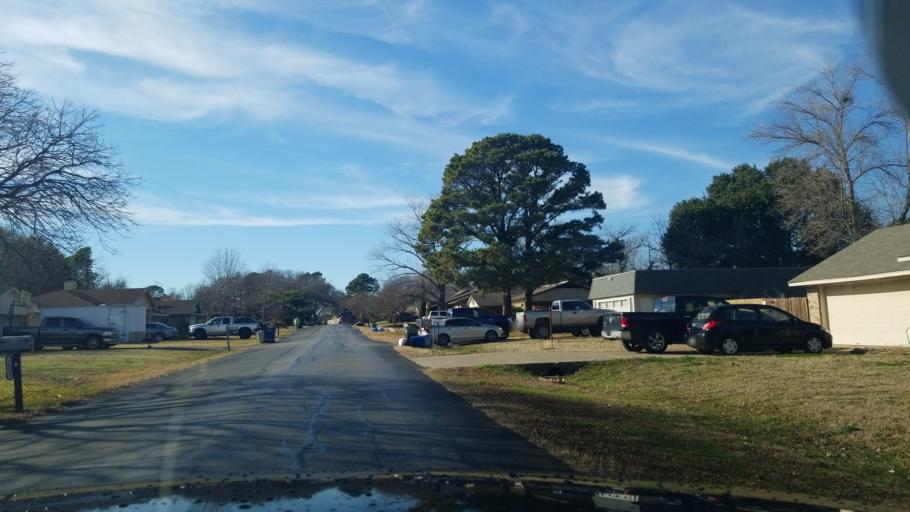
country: US
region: Texas
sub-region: Denton County
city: Corinth
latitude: 33.1505
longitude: -97.0621
